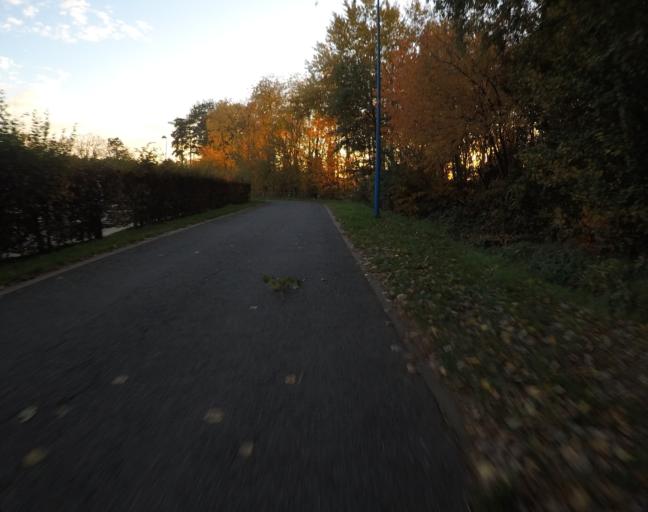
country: BE
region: Flanders
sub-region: Provincie Antwerpen
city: Herentals
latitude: 51.1783
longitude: 4.8578
